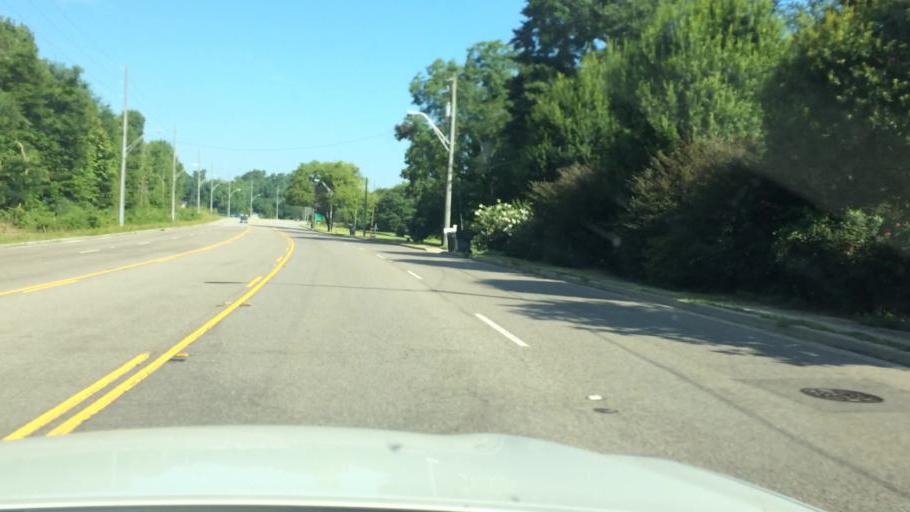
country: US
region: South Carolina
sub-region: Aiken County
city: North Augusta
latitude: 33.5295
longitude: -81.9818
